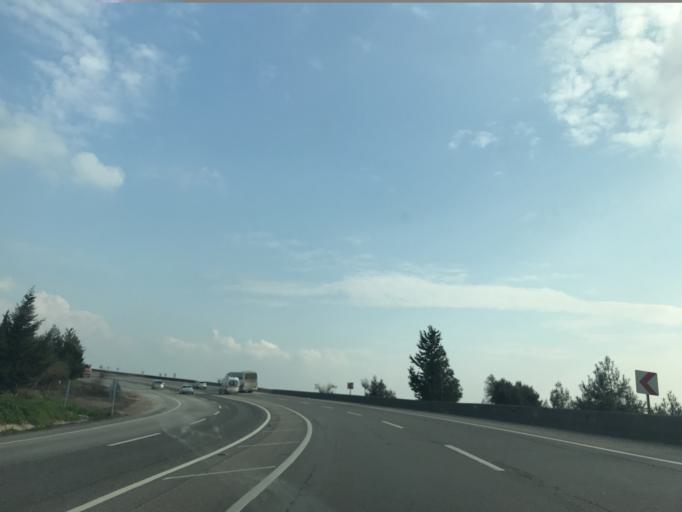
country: TR
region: Hatay
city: Belen
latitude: 36.4567
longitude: 36.2733
